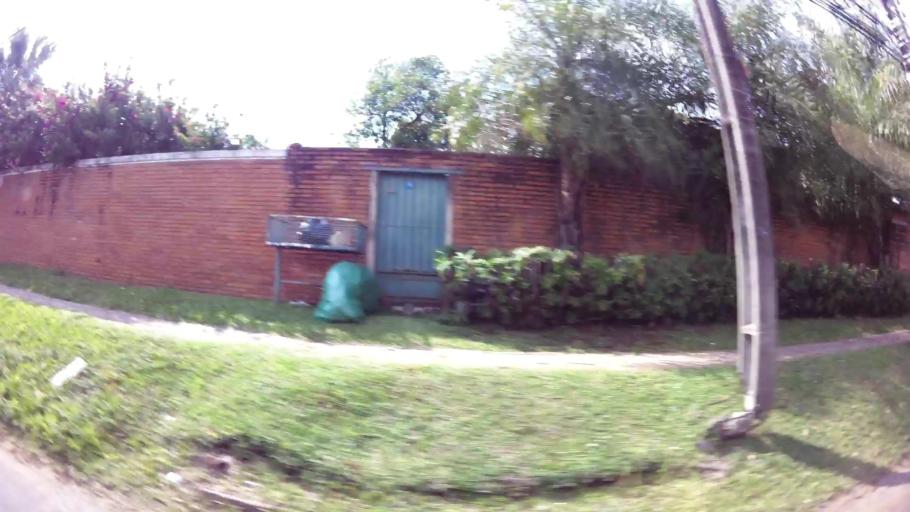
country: PY
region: Asuncion
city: Asuncion
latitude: -25.2682
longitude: -57.5624
